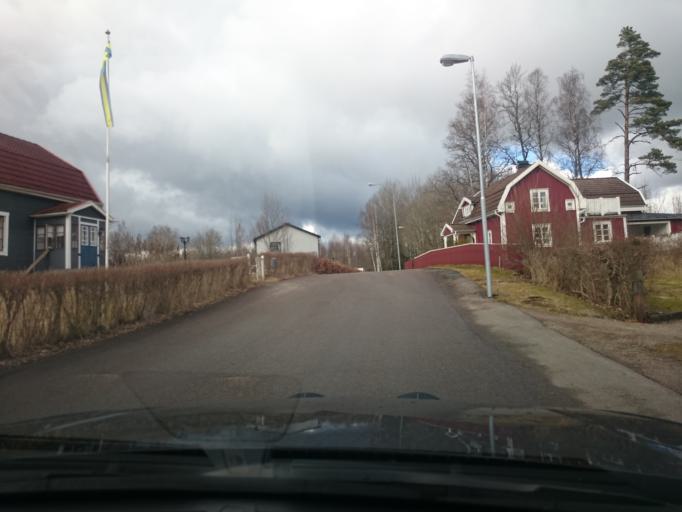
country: SE
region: Joenkoeping
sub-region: Vetlanda Kommun
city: Vetlanda
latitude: 57.3102
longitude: 15.1240
